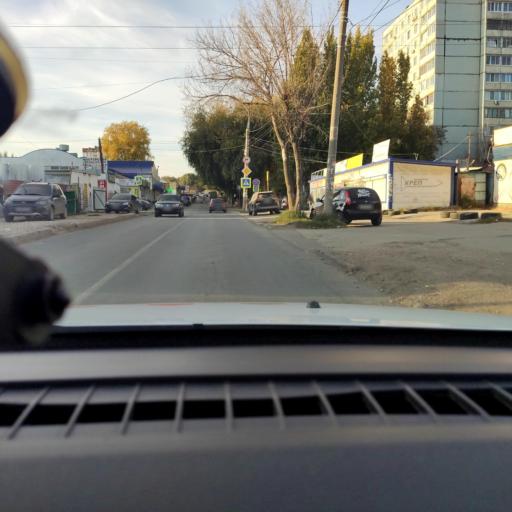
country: RU
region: Samara
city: Samara
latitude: 53.2440
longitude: 50.2540
